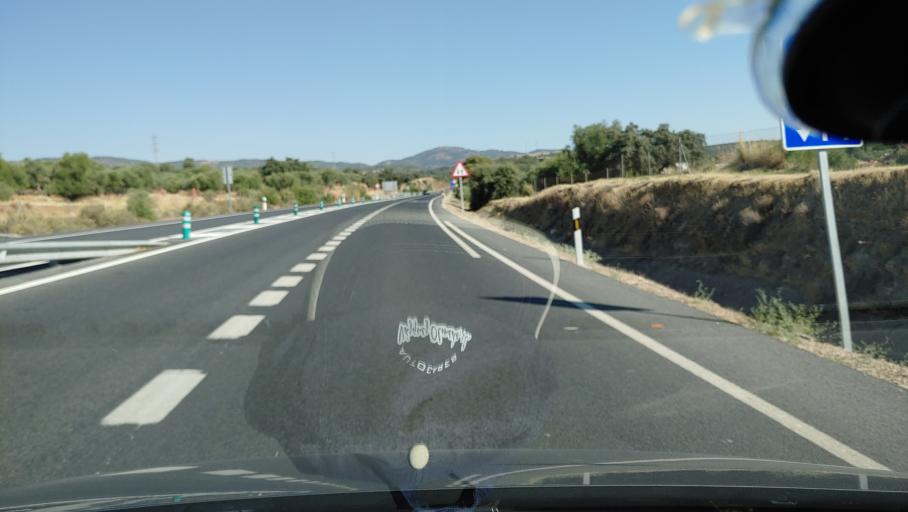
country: ES
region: Andalusia
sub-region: Province of Cordoba
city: Cordoba
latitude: 37.9226
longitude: -4.7652
